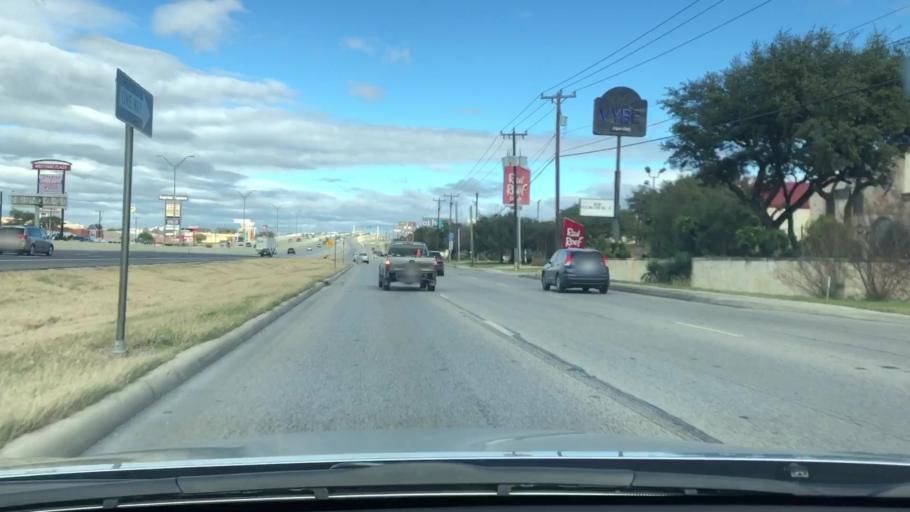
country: US
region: Texas
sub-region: Bexar County
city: Leon Valley
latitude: 29.4588
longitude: -98.6249
